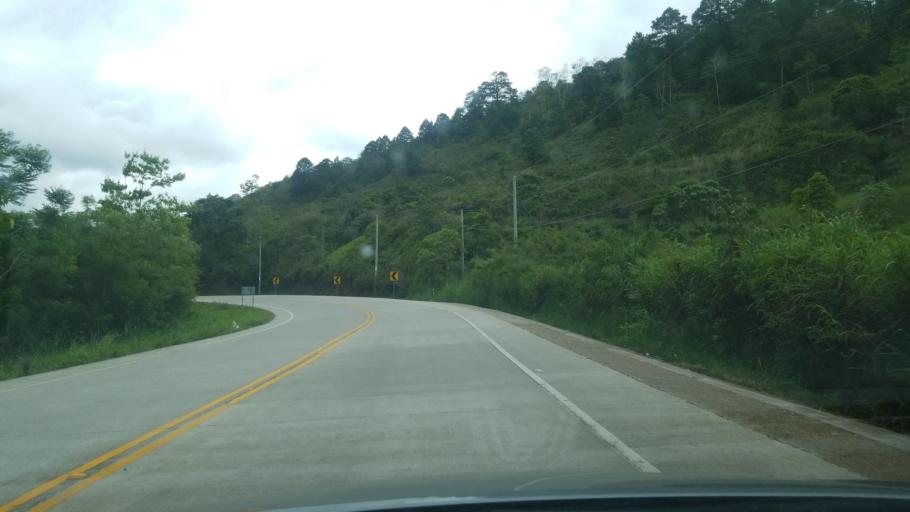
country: HN
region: Copan
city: San Jeronimo
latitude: 14.9350
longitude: -88.9282
